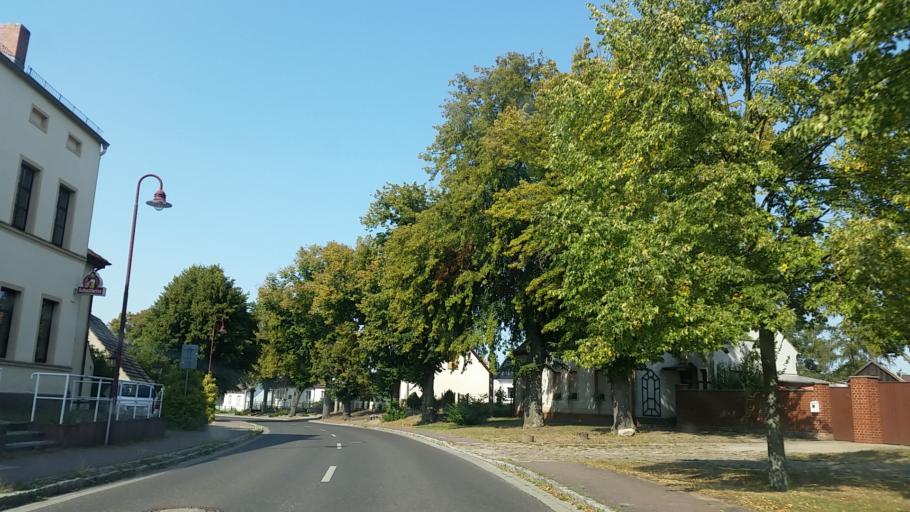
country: PL
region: West Pomeranian Voivodeship
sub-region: Powiat gryfinski
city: Cedynia
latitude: 52.8728
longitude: 14.1428
